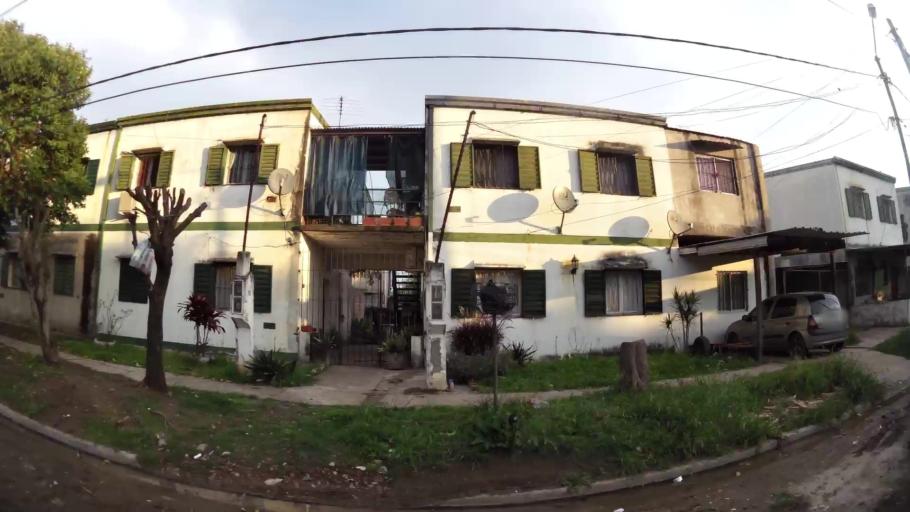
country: AR
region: Buenos Aires
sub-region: Partido de Almirante Brown
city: Adrogue
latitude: -34.7607
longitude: -58.3398
